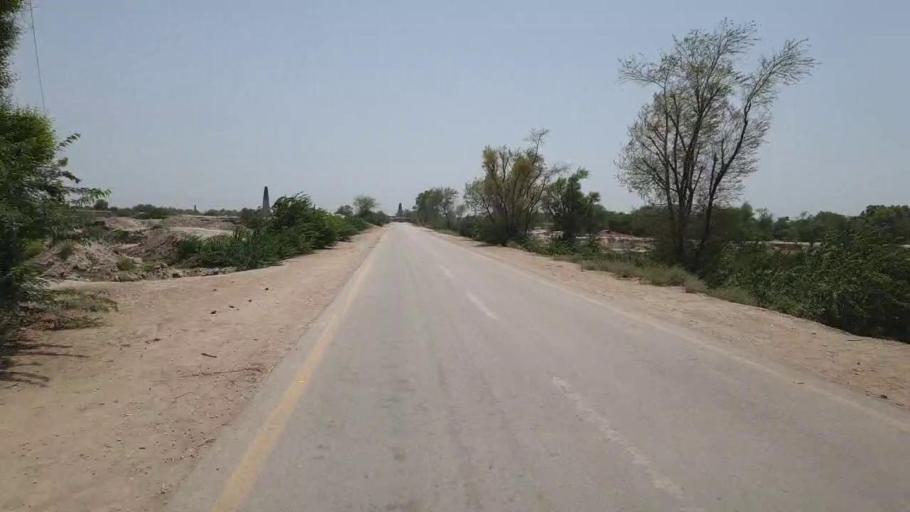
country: PK
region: Sindh
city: Daur
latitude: 26.3444
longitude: 68.1287
